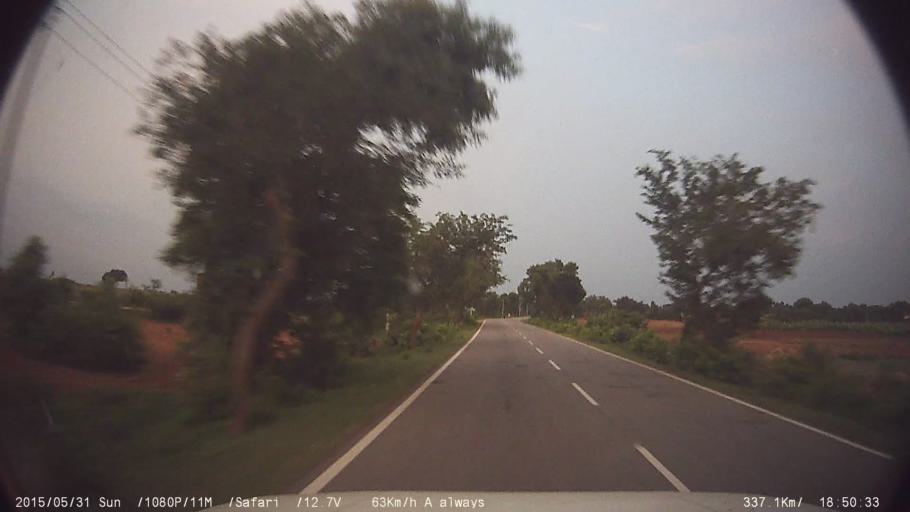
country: IN
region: Karnataka
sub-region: Mysore
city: Tirumakudal Narsipur
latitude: 12.1792
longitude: 76.8593
